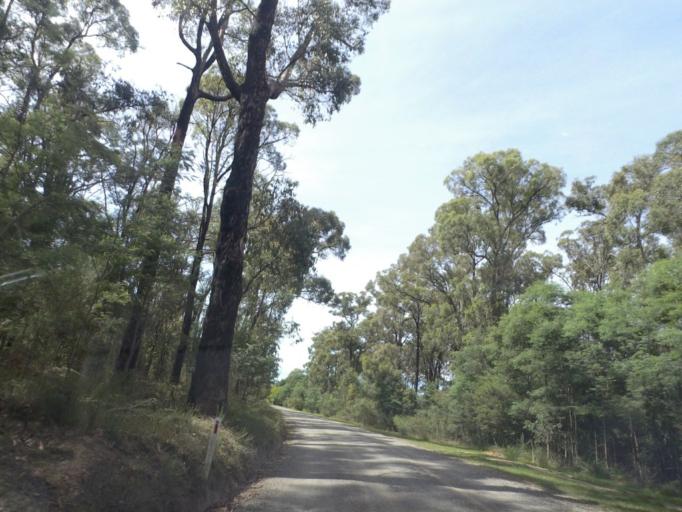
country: AU
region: Victoria
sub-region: Yarra Ranges
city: Yarra Glen
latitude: -37.5198
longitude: 145.4302
